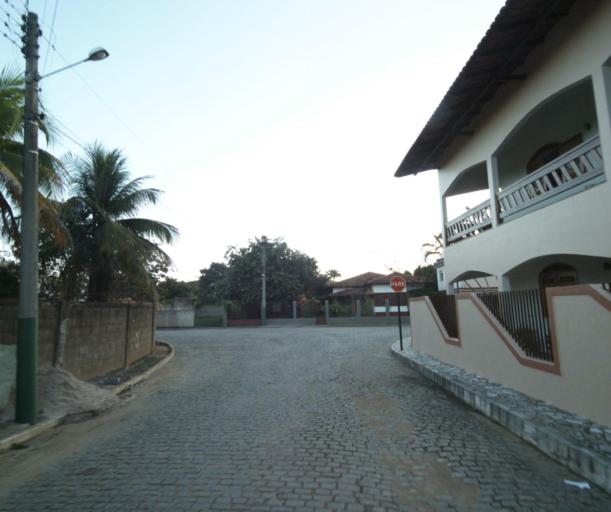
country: BR
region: Rio de Janeiro
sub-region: Bom Jesus Do Itabapoana
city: Bom Jesus do Itabapoana
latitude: -21.1558
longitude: -41.5666
